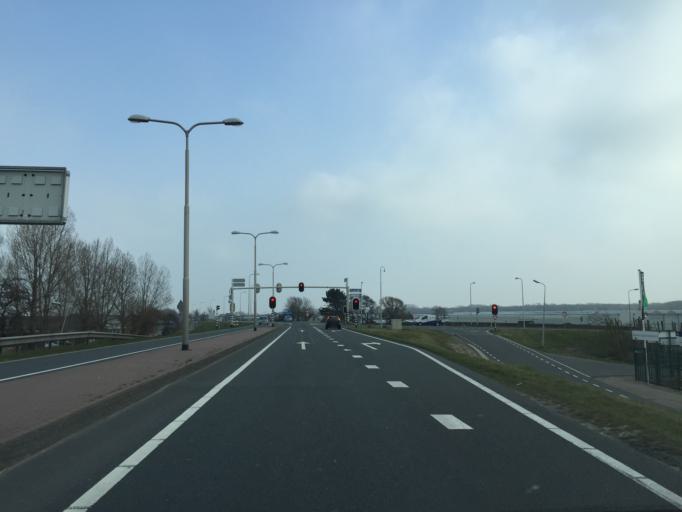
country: NL
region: South Holland
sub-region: Gemeente Westland
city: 's-Gravenzande
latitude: 51.9863
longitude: 4.1644
